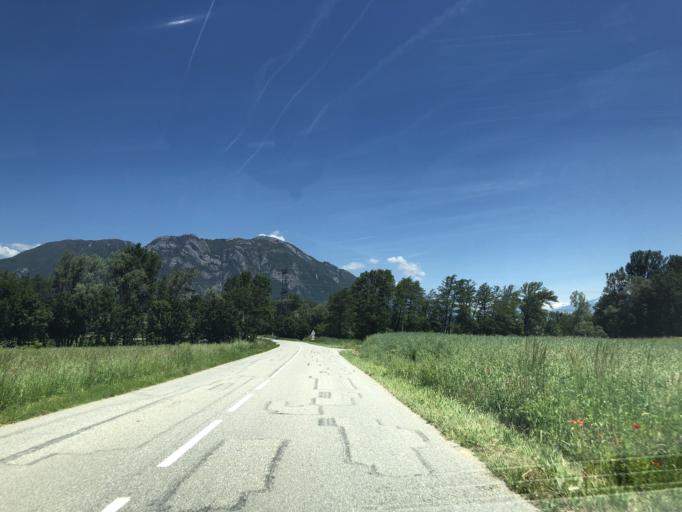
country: FR
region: Rhone-Alpes
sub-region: Departement de l'Isere
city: Chapareillan
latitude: 45.4724
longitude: 6.0069
